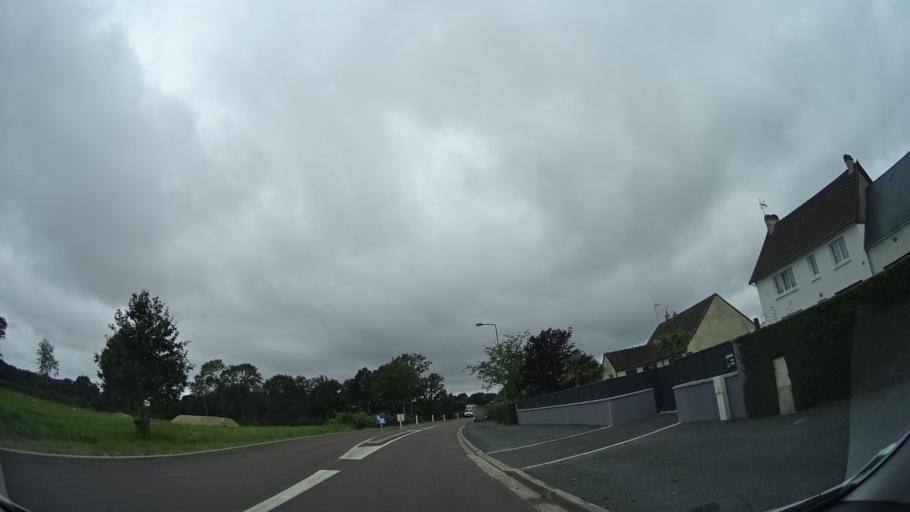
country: FR
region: Lower Normandy
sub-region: Departement de la Manche
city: La Haye-du-Puits
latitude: 49.3015
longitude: -1.5793
